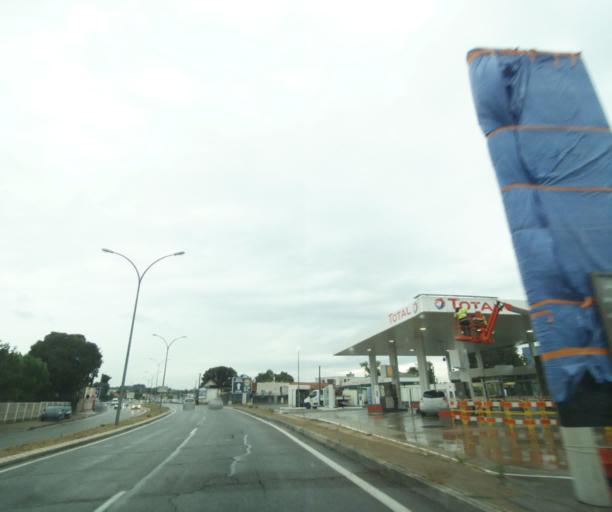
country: FR
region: Languedoc-Roussillon
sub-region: Departement du Gard
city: Rodilhan
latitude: 43.8503
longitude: 4.4004
